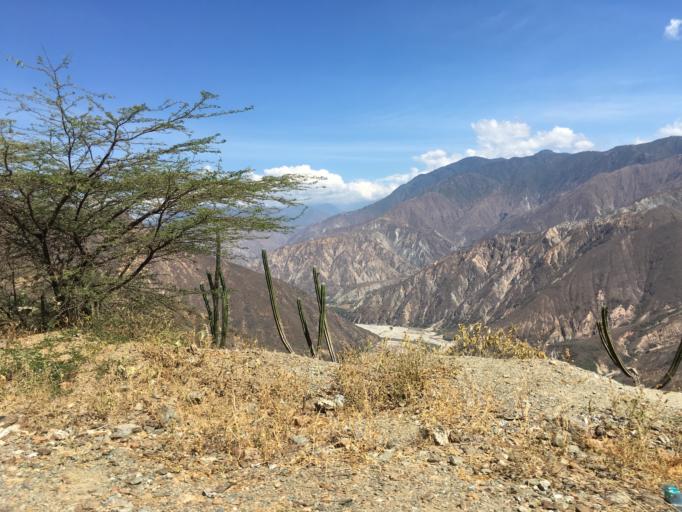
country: CO
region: Santander
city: Aratoca
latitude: 6.7714
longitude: -72.9925
